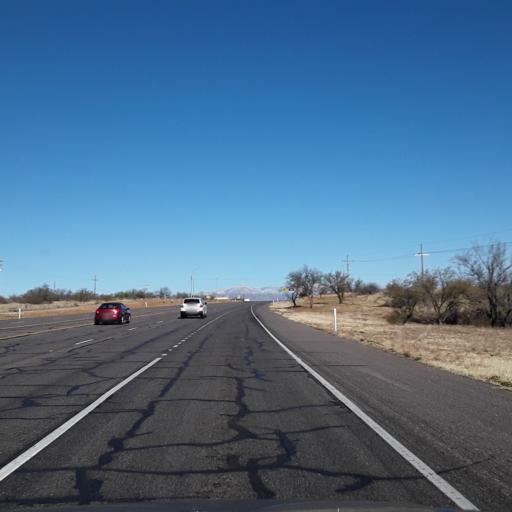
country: US
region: Arizona
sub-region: Cochise County
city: Sierra Vista
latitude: 31.5633
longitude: -110.3101
